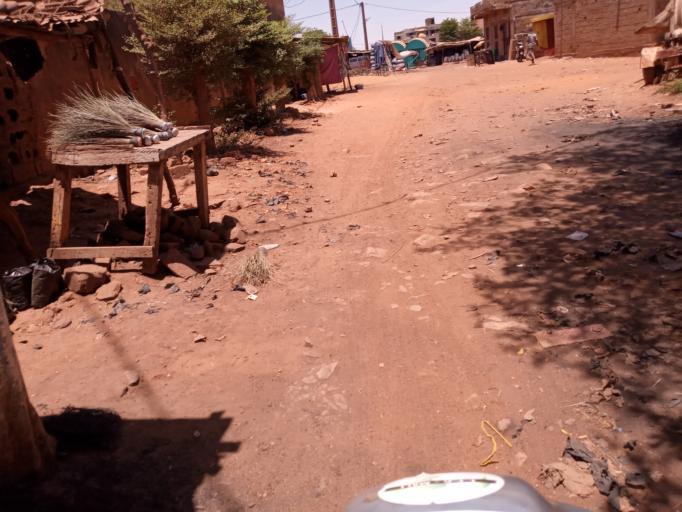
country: ML
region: Bamako
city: Bamako
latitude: 12.5830
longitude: -7.9563
